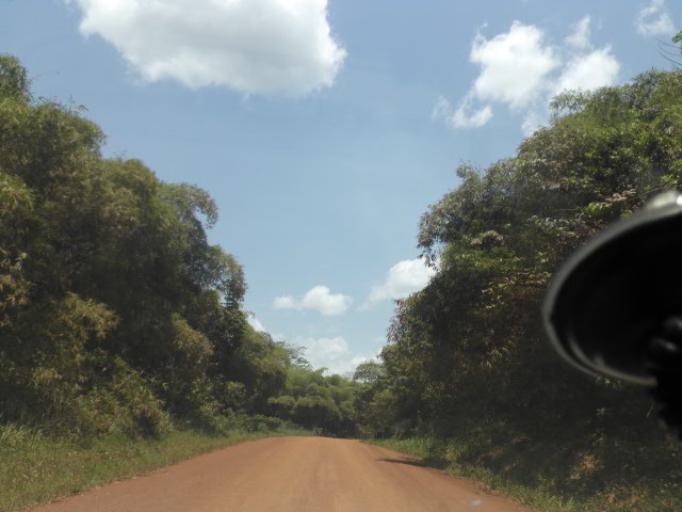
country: CD
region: Eastern Province
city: Kisangani
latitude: 0.6301
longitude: 26.0784
